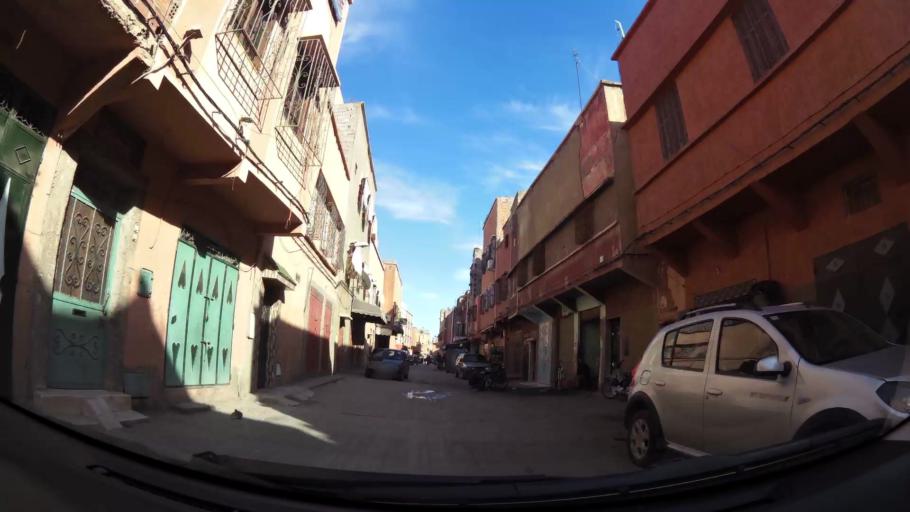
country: MA
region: Marrakech-Tensift-Al Haouz
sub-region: Marrakech
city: Marrakesh
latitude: 31.6150
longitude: -7.9641
